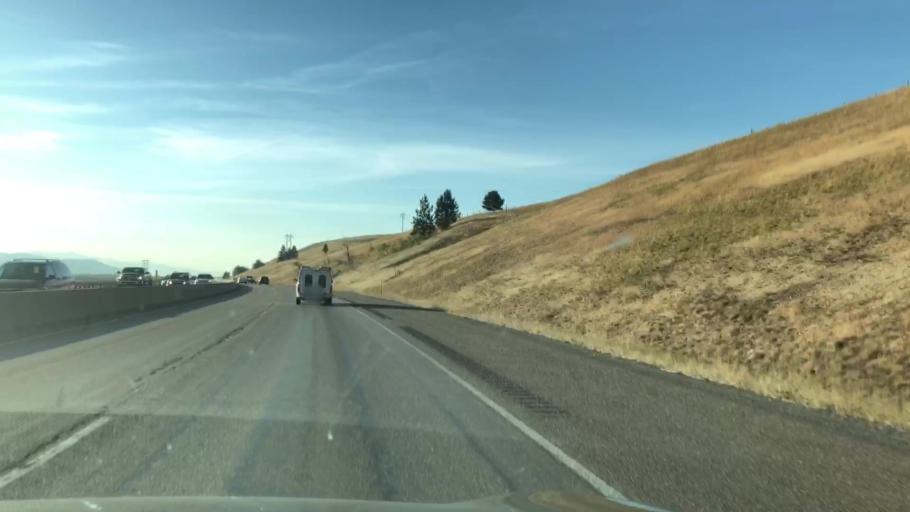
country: US
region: Montana
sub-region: Missoula County
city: Missoula
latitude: 46.8895
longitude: -113.9981
